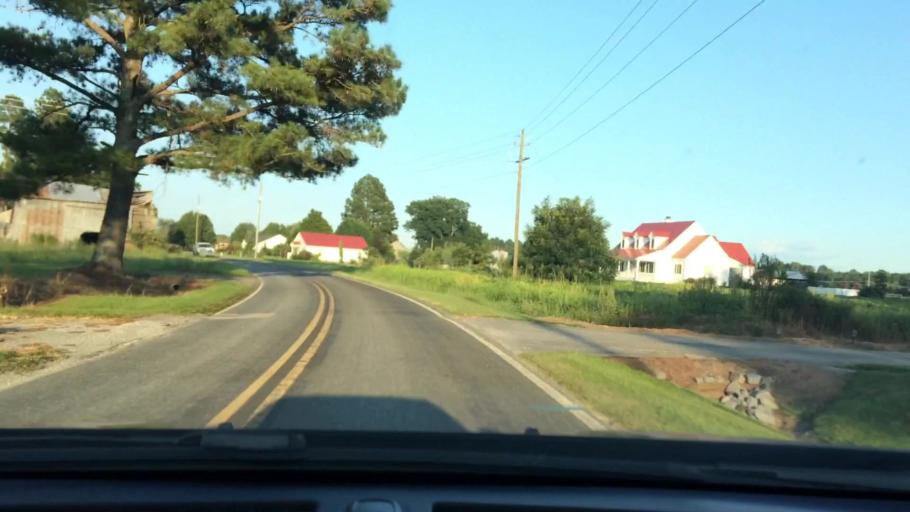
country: US
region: North Carolina
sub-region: Pitt County
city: Ayden
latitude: 35.4300
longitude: -77.4387
